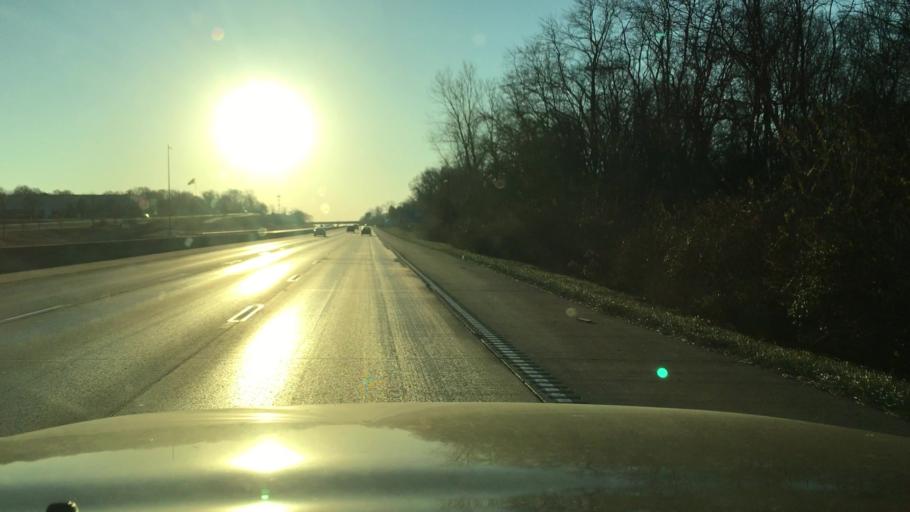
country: US
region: Missouri
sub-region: Saint Charles County
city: Saint Charles
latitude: 38.8126
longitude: -90.4898
